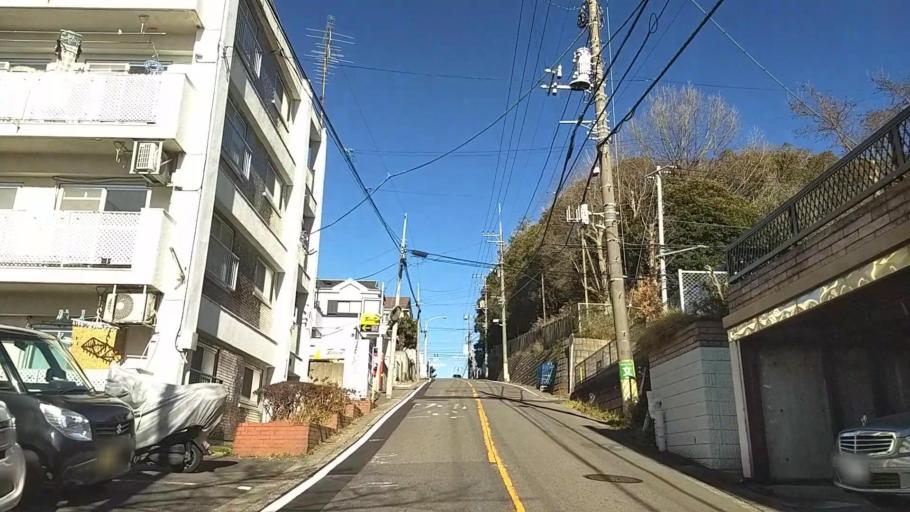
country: JP
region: Kanagawa
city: Yokohama
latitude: 35.4496
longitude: 139.5893
